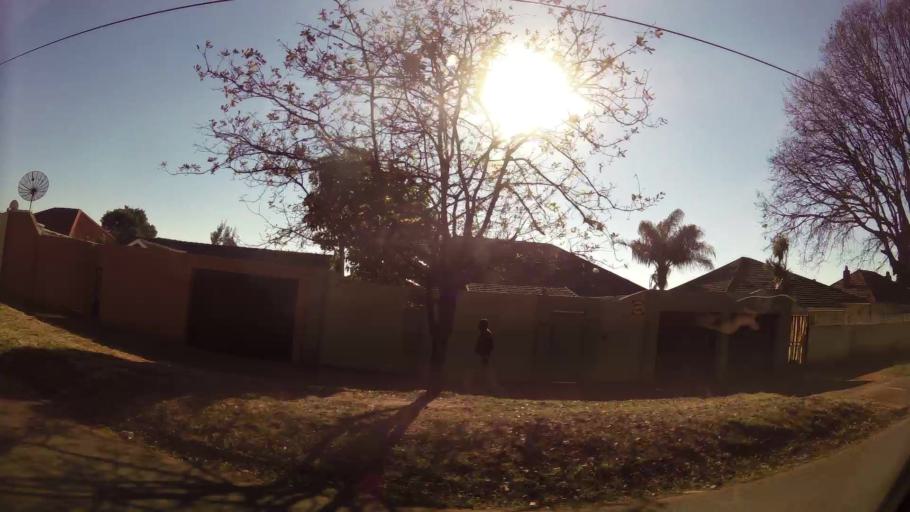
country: ZA
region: Gauteng
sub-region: City of Johannesburg Metropolitan Municipality
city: Johannesburg
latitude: -26.1947
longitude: 28.0937
